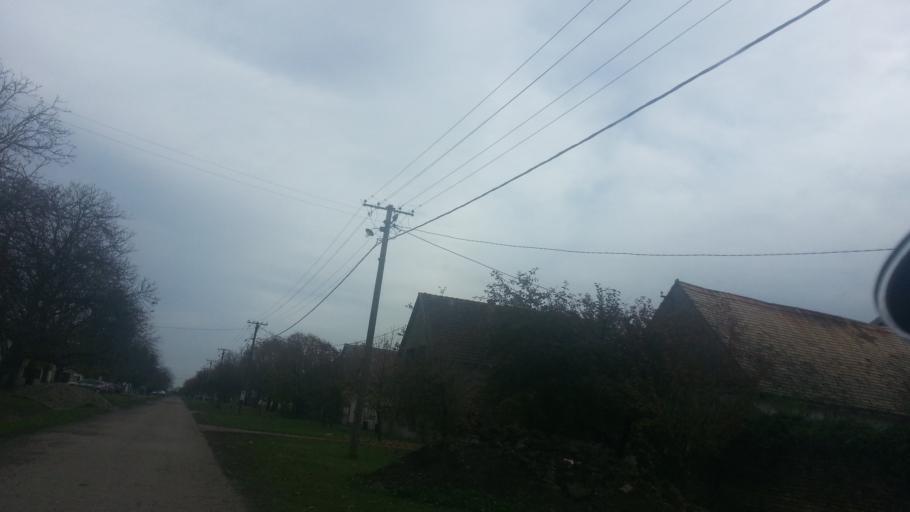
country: RS
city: Golubinci
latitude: 44.9906
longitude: 20.0744
